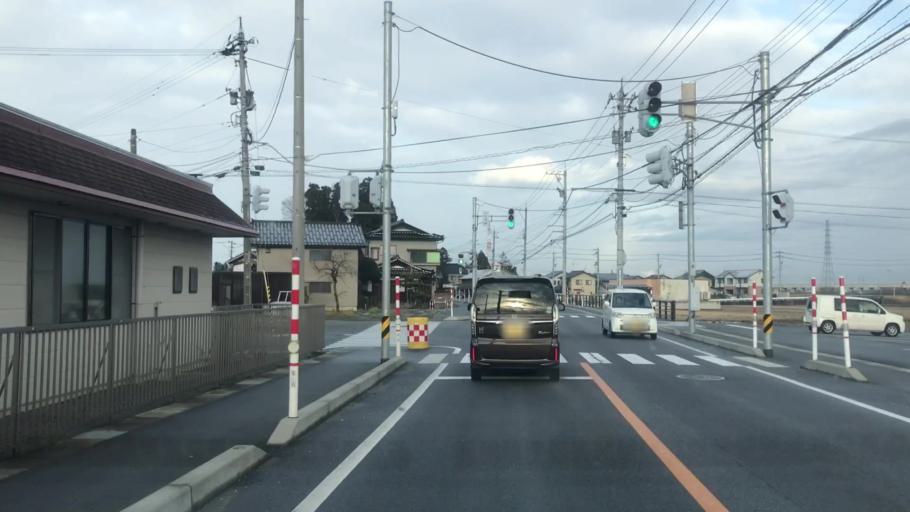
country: JP
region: Toyama
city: Kamiichi
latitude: 36.7059
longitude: 137.3095
